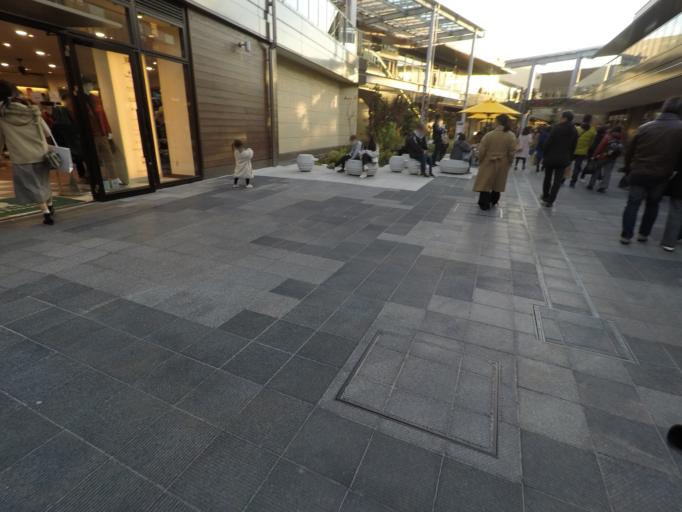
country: JP
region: Kanagawa
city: Minami-rinkan
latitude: 35.5092
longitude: 139.4726
